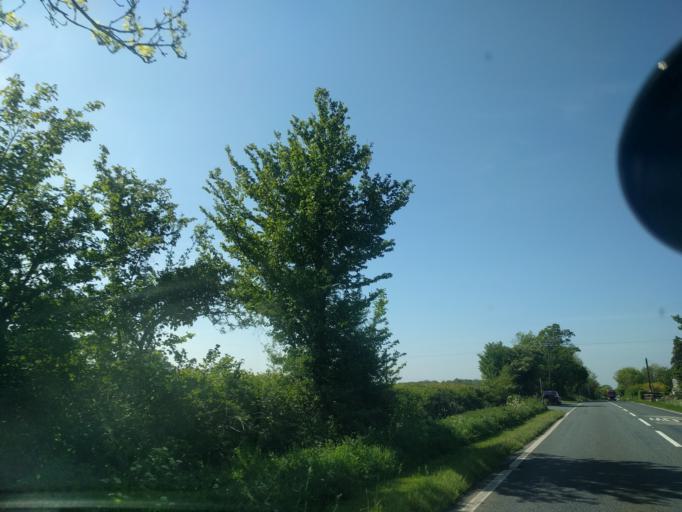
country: GB
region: England
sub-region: Somerset
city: Castle Cary
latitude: 51.1010
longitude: -2.5956
